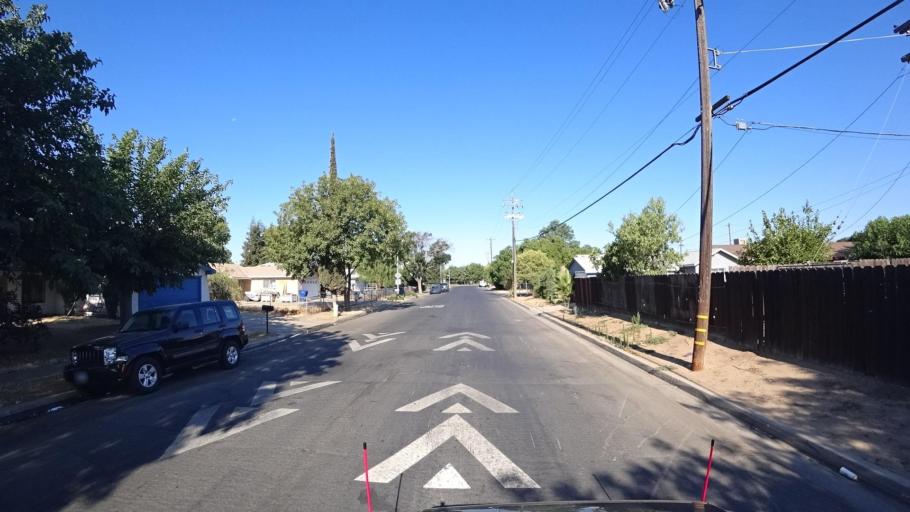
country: US
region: California
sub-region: Fresno County
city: Fresno
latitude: 36.7105
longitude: -119.7440
